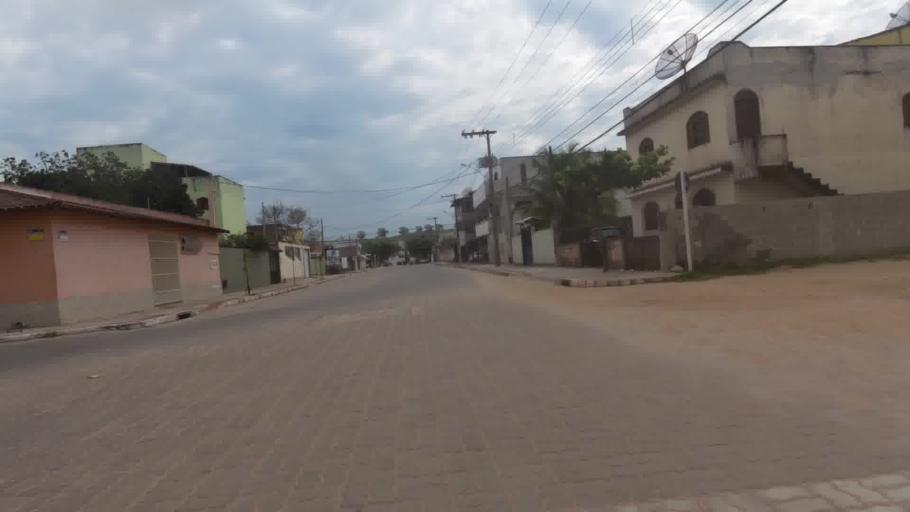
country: BR
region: Espirito Santo
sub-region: Piuma
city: Piuma
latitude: -20.8426
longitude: -40.7428
